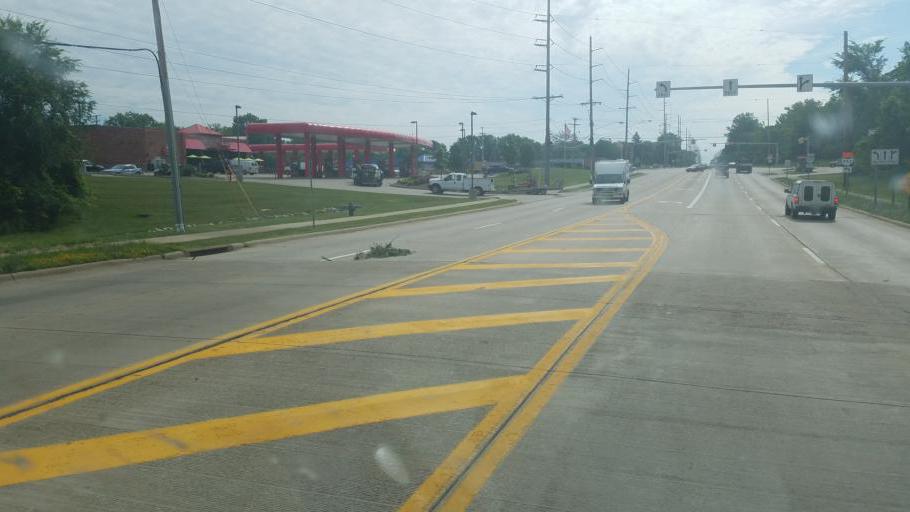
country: US
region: Ohio
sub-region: Cuyahoga County
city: Strongsville
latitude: 41.3124
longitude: -81.8599
